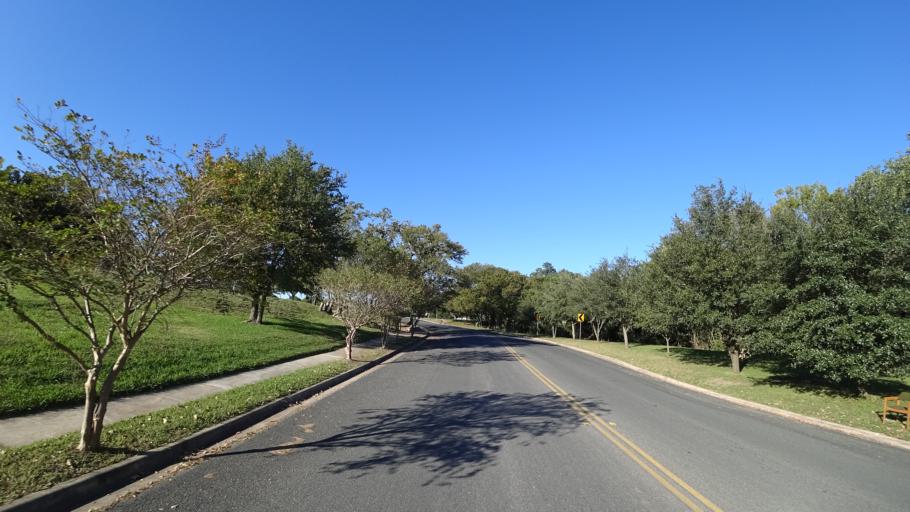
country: US
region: Texas
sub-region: Travis County
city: Austin
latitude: 30.3057
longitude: -97.6752
